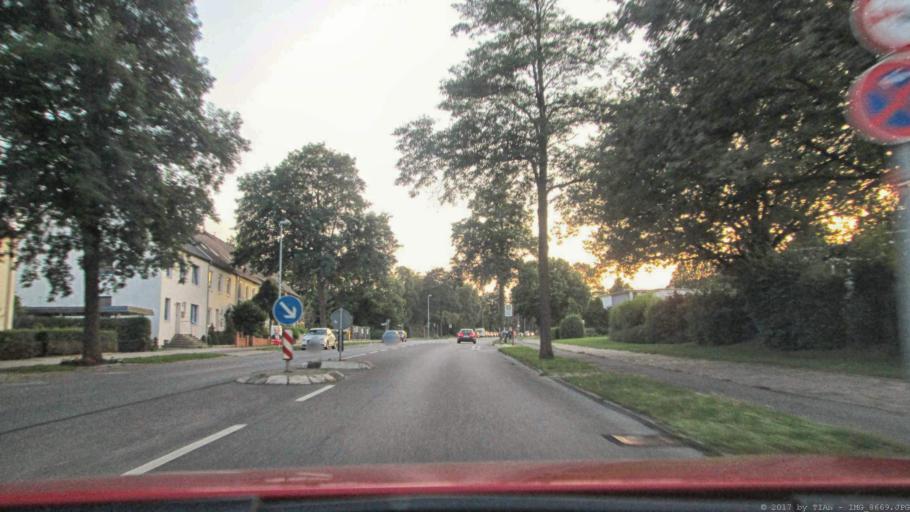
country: DE
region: Lower Saxony
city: Wolfsburg
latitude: 52.4101
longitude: 10.7760
